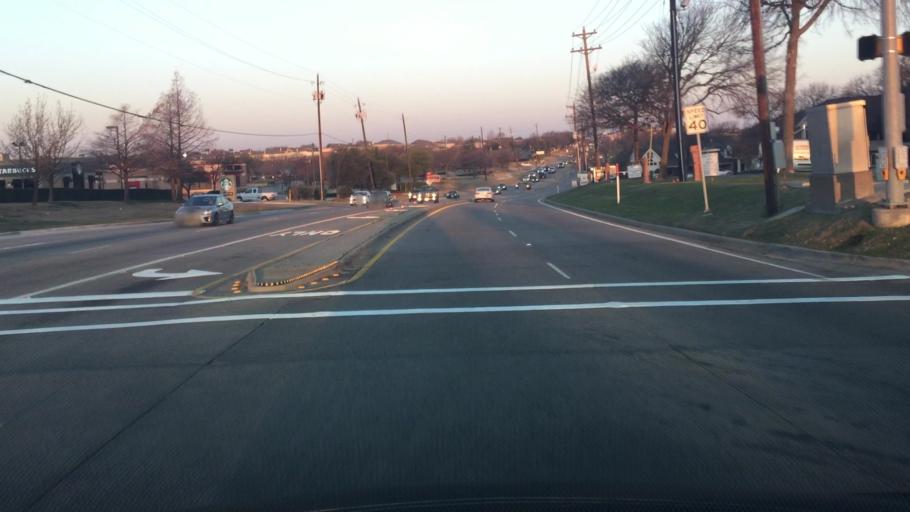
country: US
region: Texas
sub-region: Denton County
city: Highland Village
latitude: 33.0716
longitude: -97.0578
